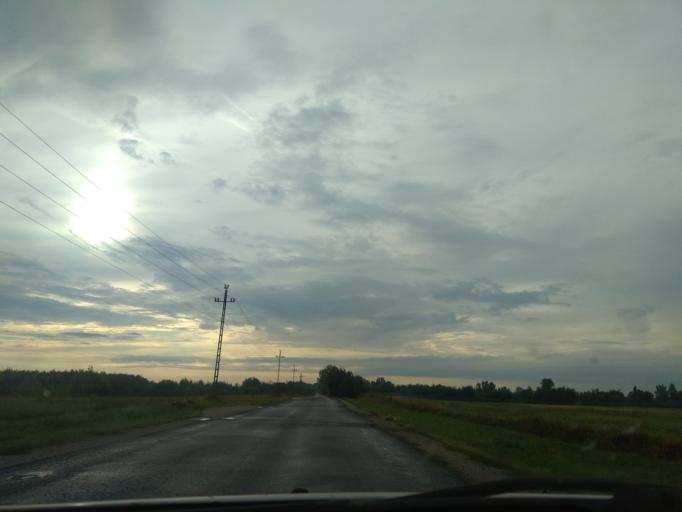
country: HU
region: Borsod-Abauj-Zemplen
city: Onga
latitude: 48.1169
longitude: 20.9350
